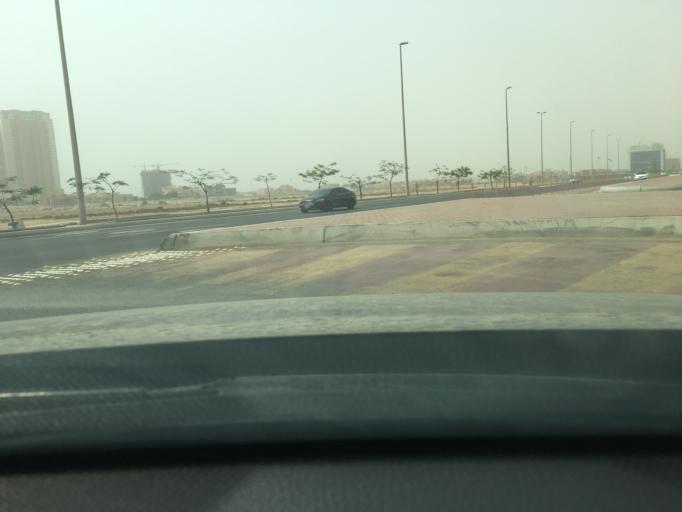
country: SA
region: Makkah
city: Jeddah
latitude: 21.6407
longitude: 39.1117
